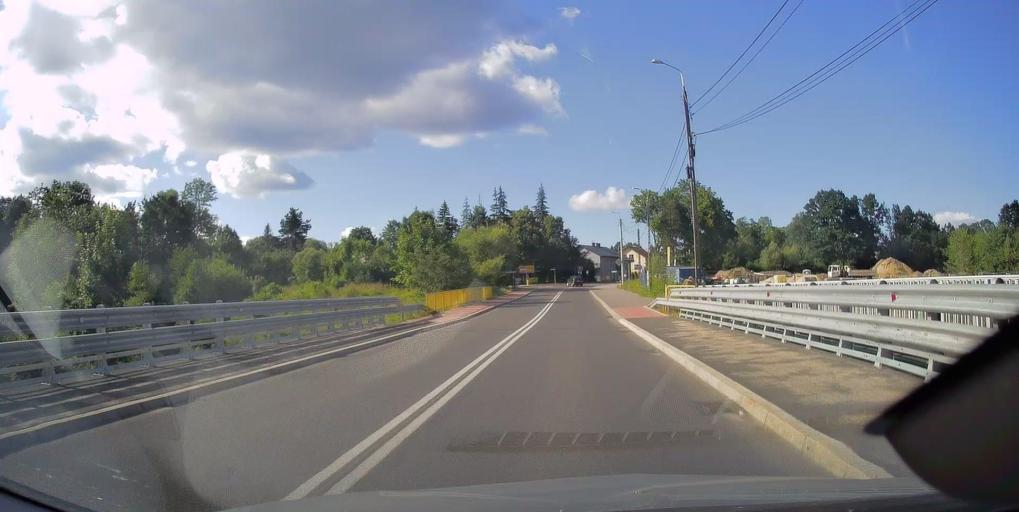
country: PL
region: Swietokrzyskie
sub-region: Powiat skarzyski
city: Suchedniow
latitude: 51.0383
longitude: 20.8357
